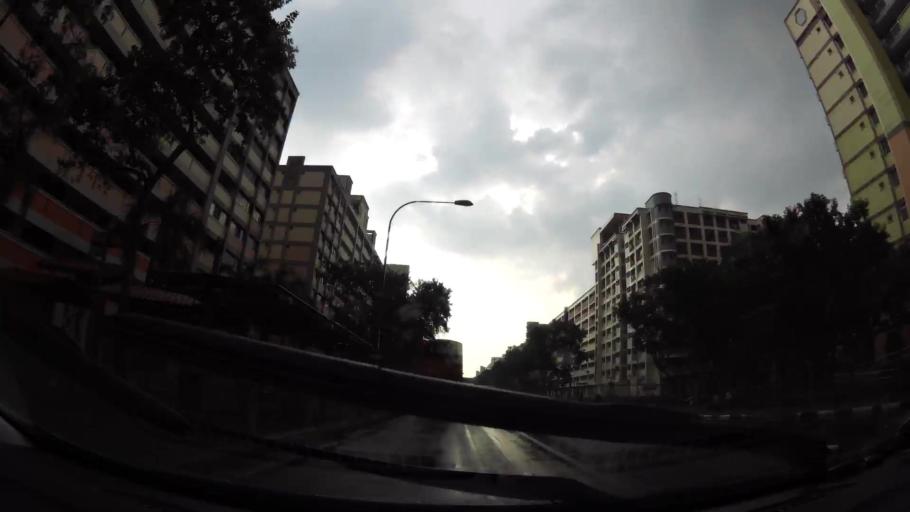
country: SG
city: Singapore
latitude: 1.3441
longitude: 103.9559
